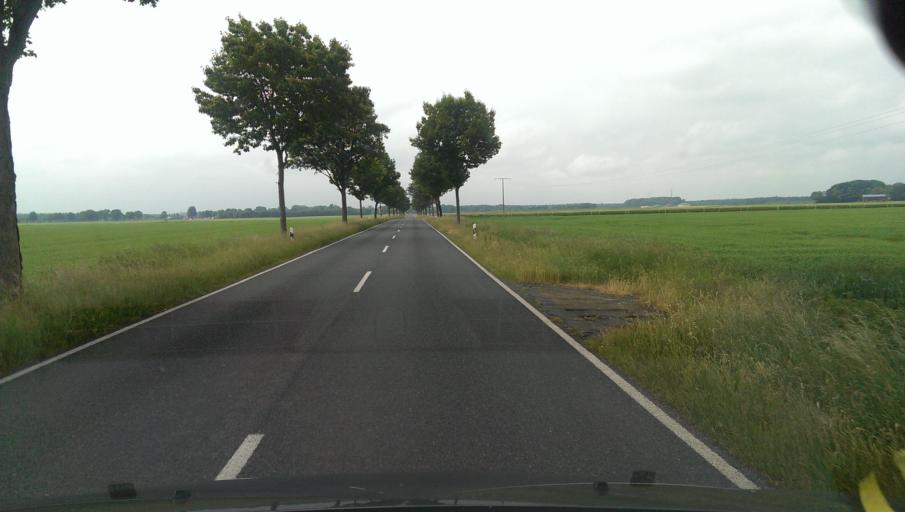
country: DE
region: Lower Saxony
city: Sprakensehl
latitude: 52.7568
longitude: 10.5086
